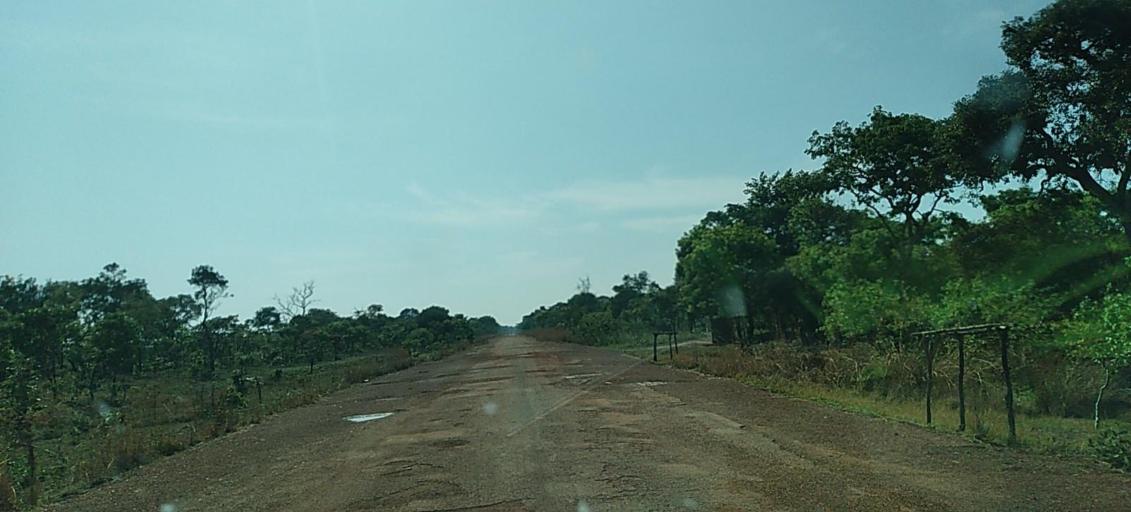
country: ZM
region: North-Western
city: Mwinilunga
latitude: -11.7887
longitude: 25.0568
